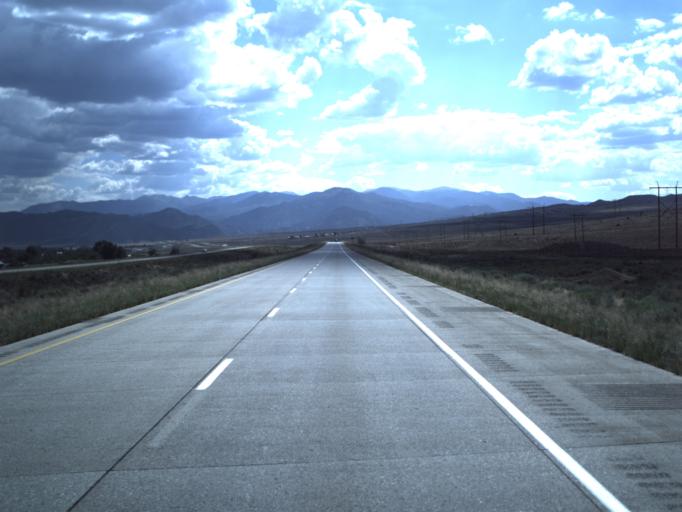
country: US
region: Utah
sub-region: Sevier County
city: Monroe
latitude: 38.6518
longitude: -112.2124
